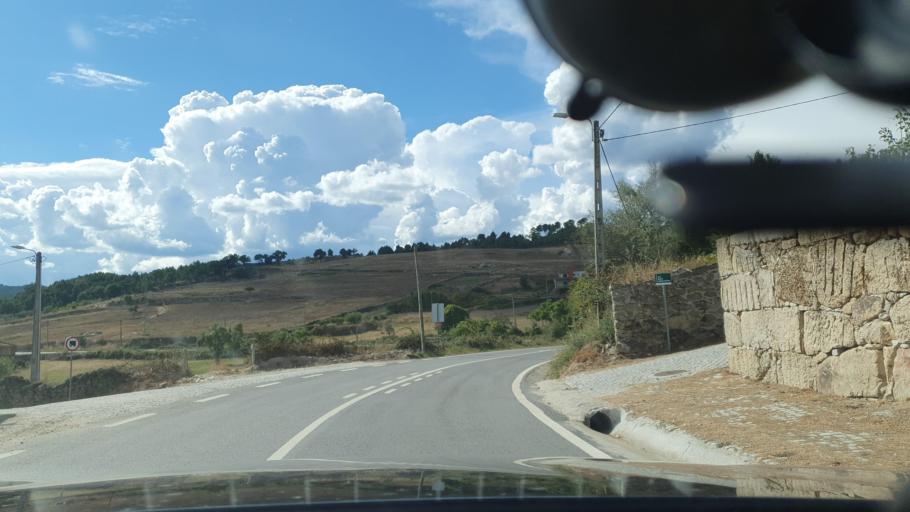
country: PT
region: Vila Real
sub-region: Chaves
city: Chaves
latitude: 41.7112
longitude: -7.5644
